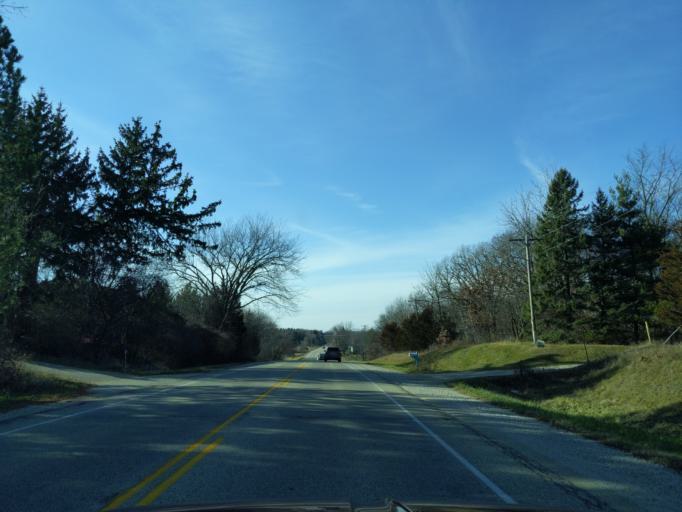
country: US
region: Wisconsin
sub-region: Walworth County
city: Whitewater
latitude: 42.8281
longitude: -88.8133
